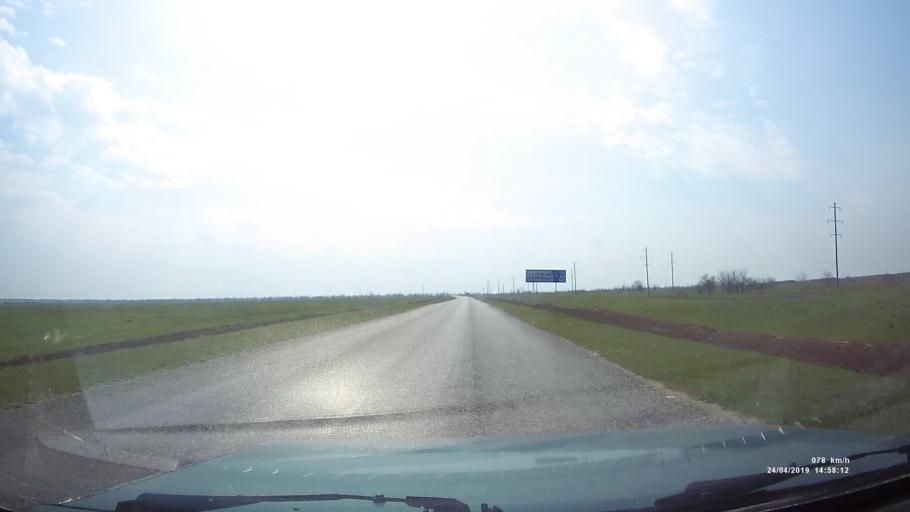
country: RU
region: Rostov
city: Remontnoye
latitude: 46.5698
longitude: 43.6009
